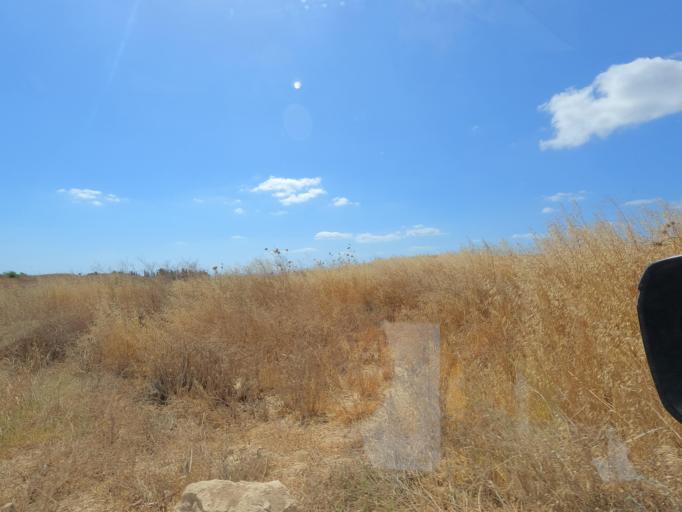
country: CY
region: Pafos
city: Paphos
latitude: 34.7400
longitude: 32.5020
